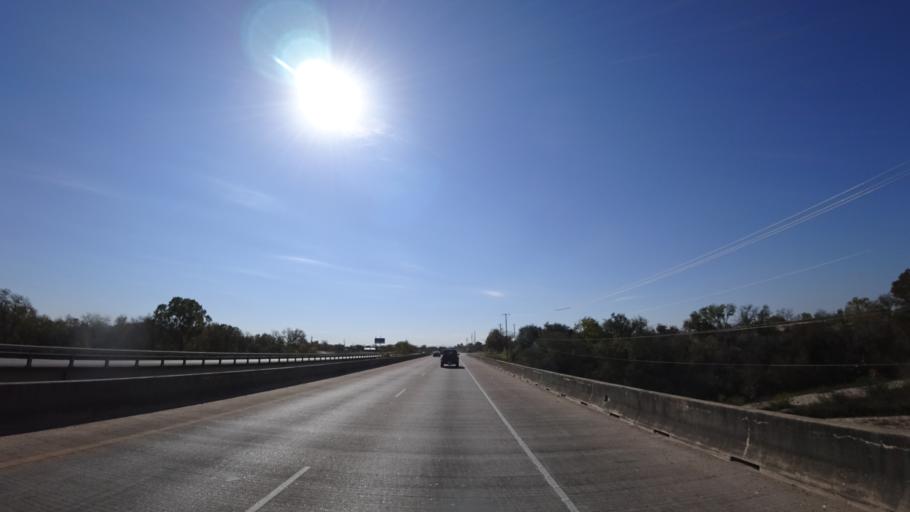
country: US
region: Texas
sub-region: Travis County
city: Austin
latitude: 30.1786
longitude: -97.6890
